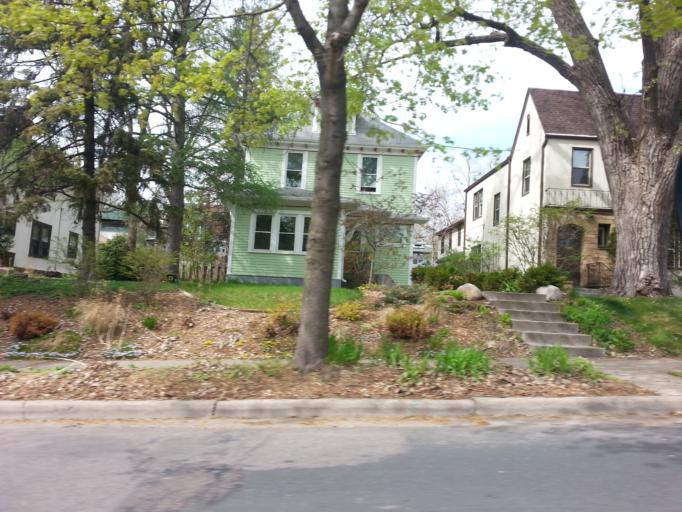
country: US
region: Minnesota
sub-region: Ramsey County
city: Lauderdale
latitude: 44.9646
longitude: -93.2132
